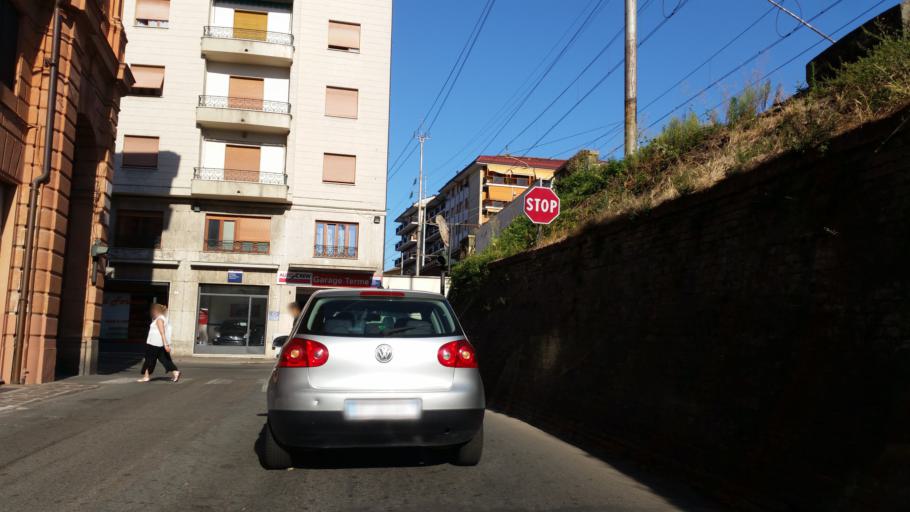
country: IT
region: Piedmont
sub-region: Provincia di Alessandria
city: Acqui Terme
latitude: 44.6723
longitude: 8.4684
